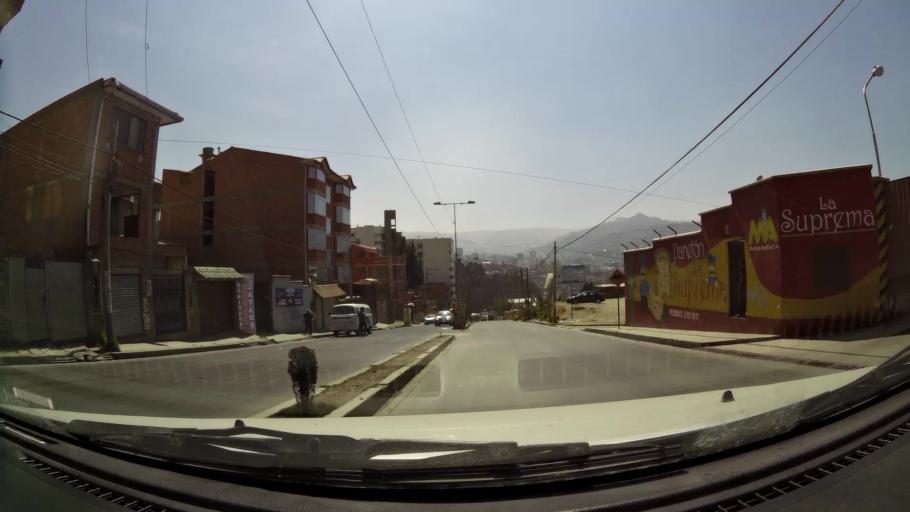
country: BO
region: La Paz
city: La Paz
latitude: -16.5276
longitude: -68.1238
